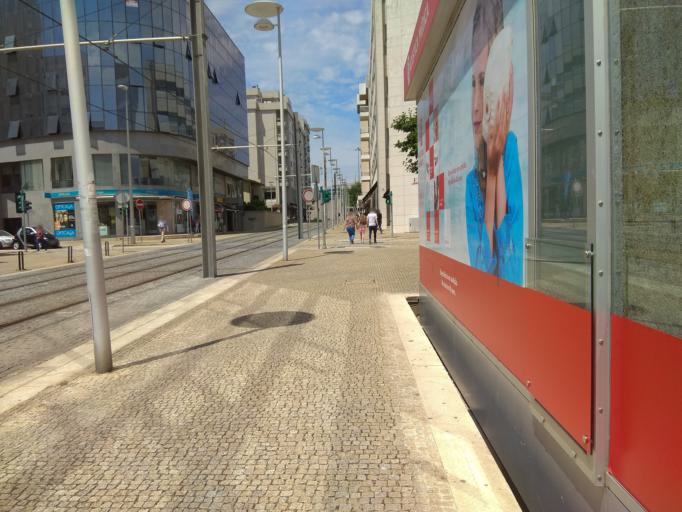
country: PT
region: Porto
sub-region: Maia
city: Maia
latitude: 41.2311
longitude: -8.6226
